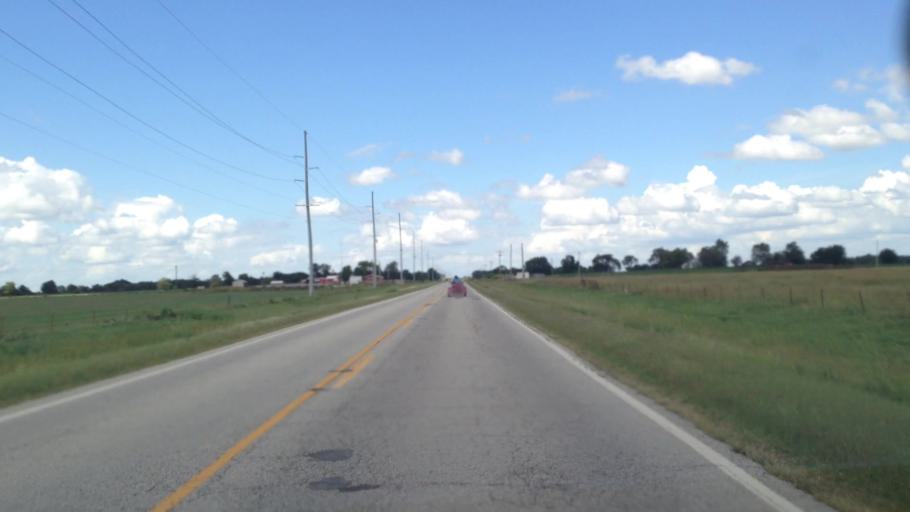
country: US
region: Kansas
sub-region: Labette County
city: Chetopa
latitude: 36.9000
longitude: -95.0895
